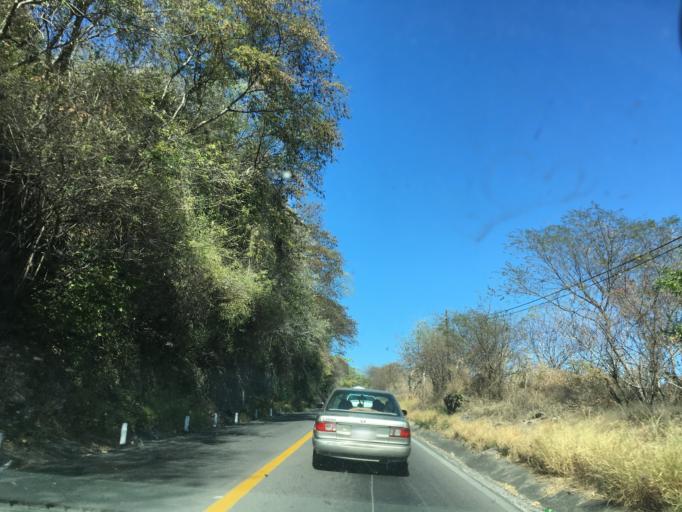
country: MX
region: Michoacan
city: Nueva Italia de Ruiz
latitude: 19.0828
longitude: -102.0622
